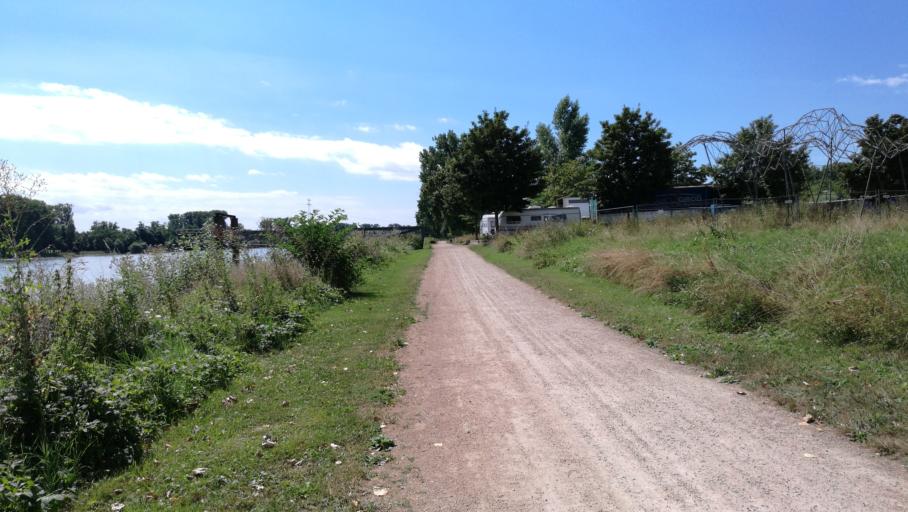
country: DE
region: Baden-Wuerttemberg
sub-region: Freiburg Region
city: Kehl
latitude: 48.5662
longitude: 7.8026
